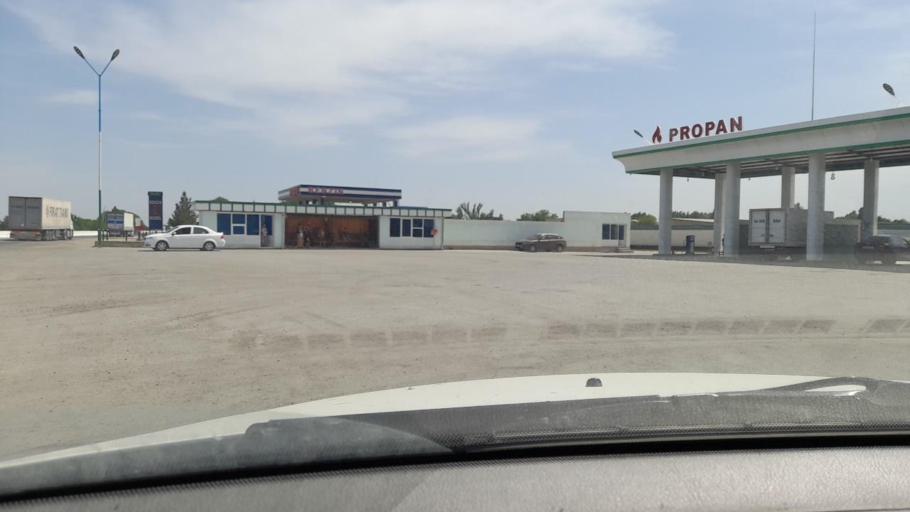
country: UZ
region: Navoiy
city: Navoiy
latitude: 40.0770
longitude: 65.6131
